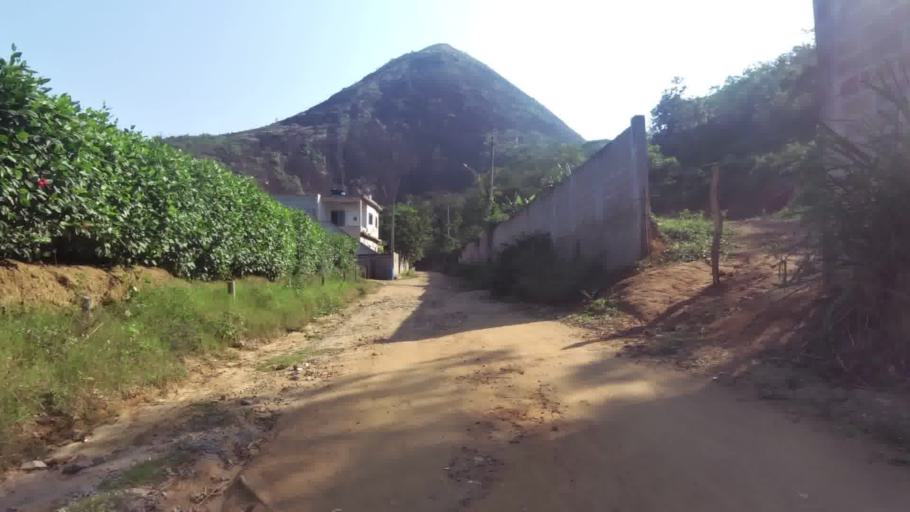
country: BR
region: Espirito Santo
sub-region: Piuma
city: Piuma
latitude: -20.8656
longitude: -40.7620
